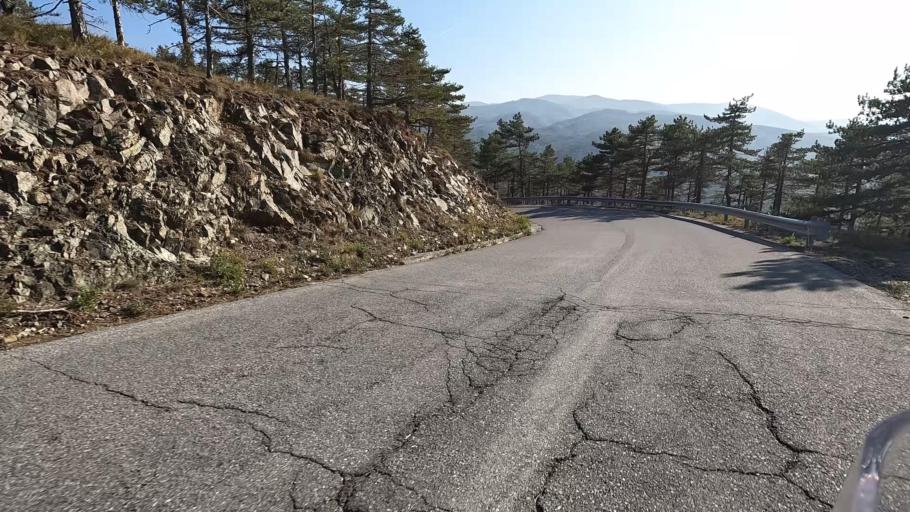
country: IT
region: Liguria
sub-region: Provincia di Savona
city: Sassello
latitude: 44.5040
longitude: 8.5368
